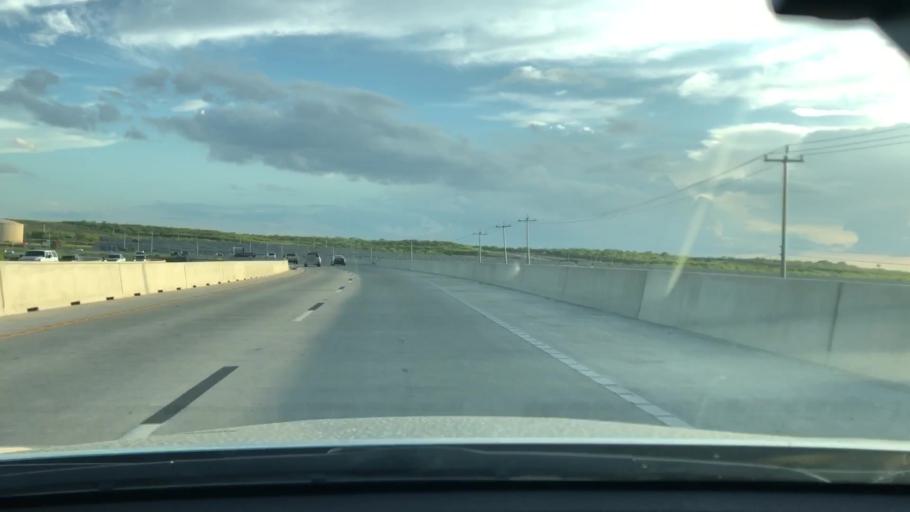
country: US
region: Texas
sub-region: Bexar County
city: Converse
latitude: 29.4844
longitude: -98.2951
